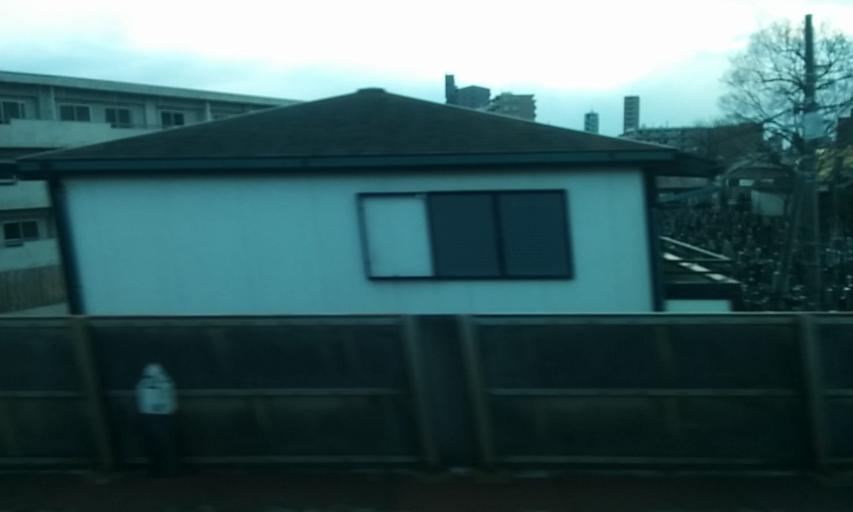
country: JP
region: Saitama
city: Kawaguchi
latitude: 35.7869
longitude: 139.7171
